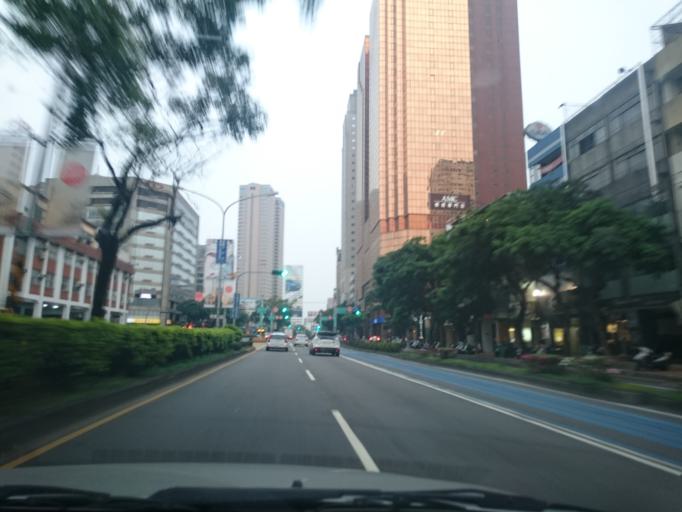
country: TW
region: Taiwan
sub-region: Taichung City
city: Taichung
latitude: 24.1543
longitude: 120.6647
